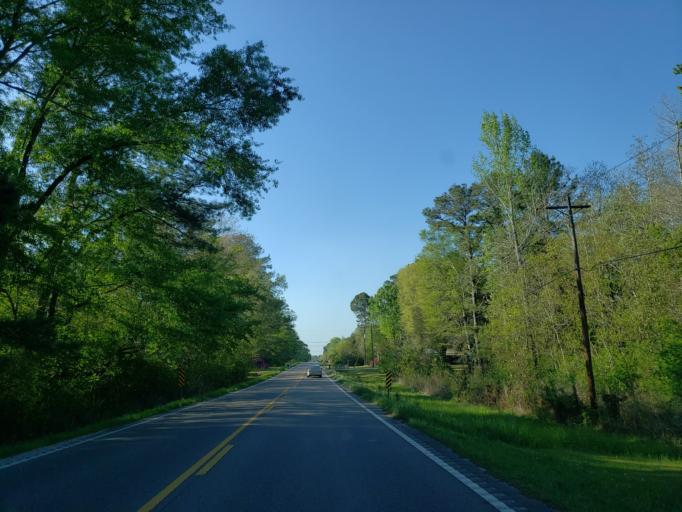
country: US
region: Mississippi
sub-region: Jones County
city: Laurel
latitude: 31.6338
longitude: -89.0933
